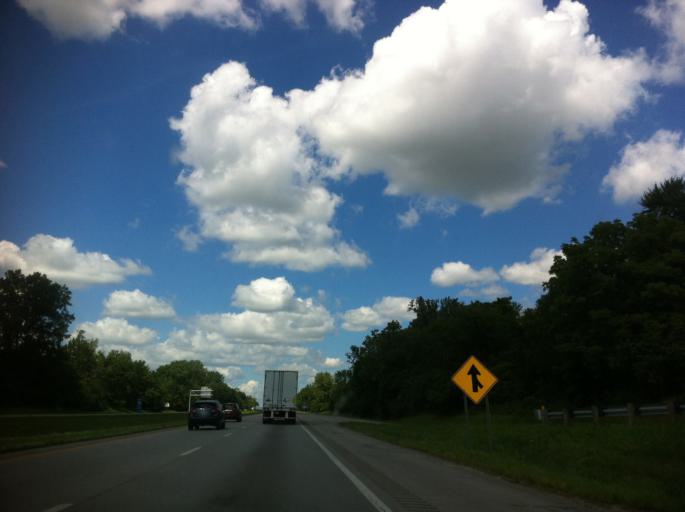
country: US
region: Ohio
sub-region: Lucas County
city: Sylvania
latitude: 41.7162
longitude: -83.6882
